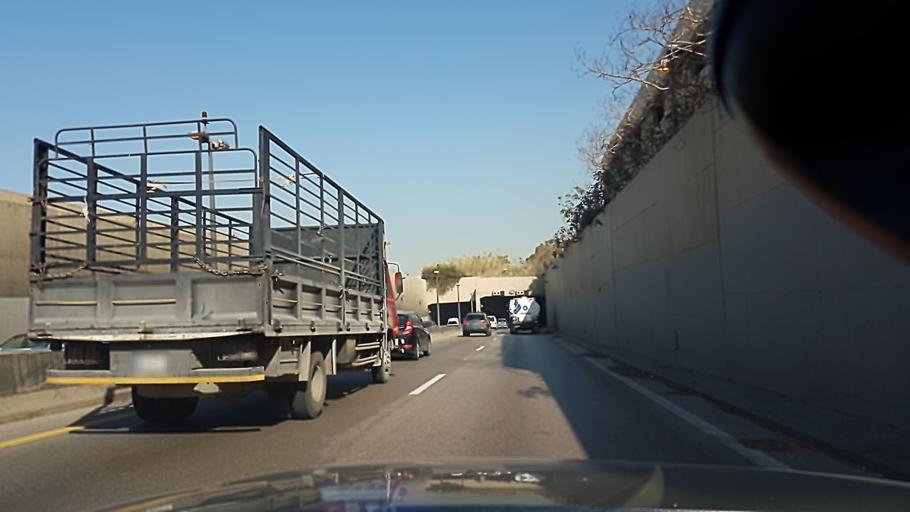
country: LB
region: Mont-Liban
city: Baabda
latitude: 33.8187
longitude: 35.4989
